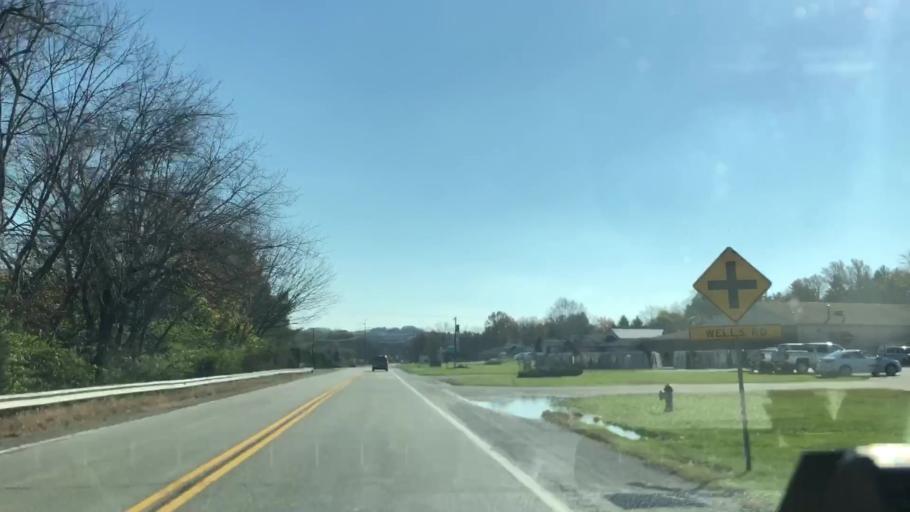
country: US
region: Pennsylvania
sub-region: Montgomery County
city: Sanatoga
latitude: 40.2046
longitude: -75.5893
